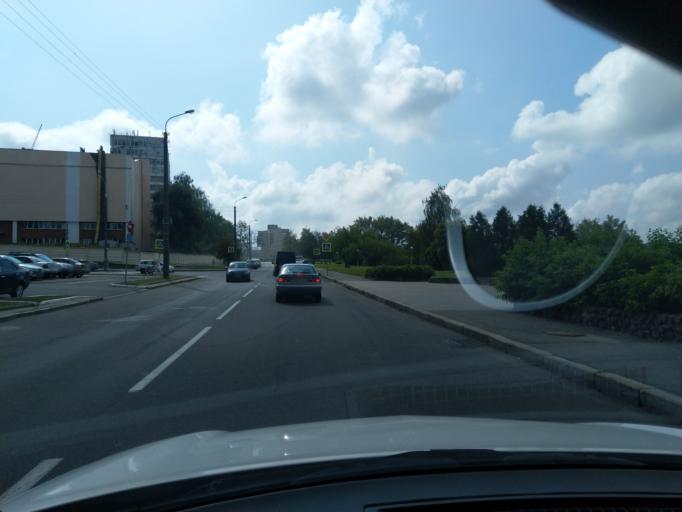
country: BY
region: Minsk
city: Minsk
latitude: 53.8939
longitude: 27.5832
